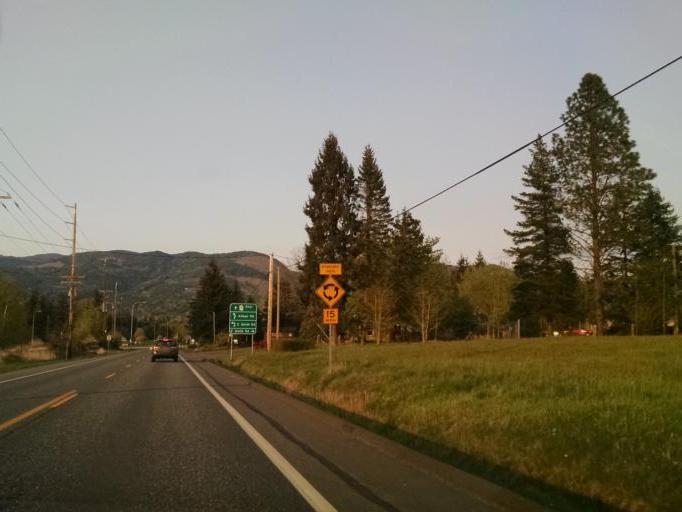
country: US
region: Washington
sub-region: Whatcom County
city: Everson
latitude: 48.8304
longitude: -122.3081
